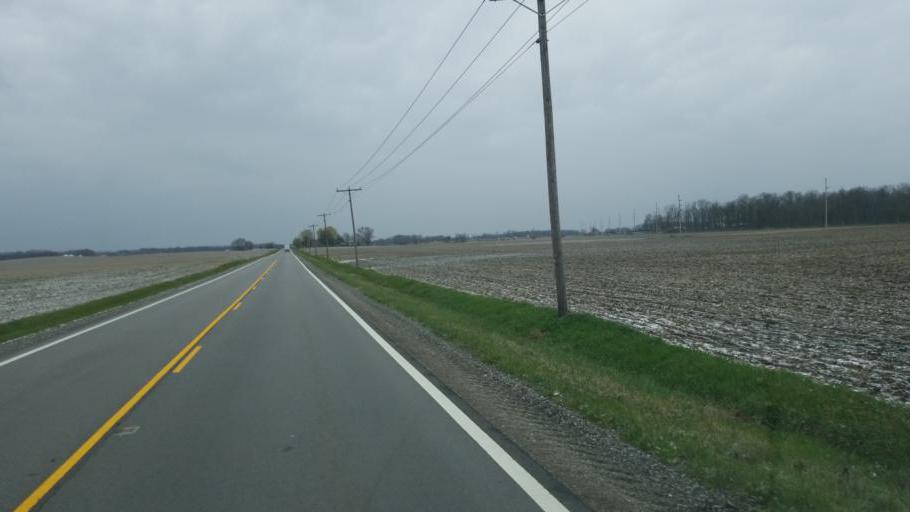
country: US
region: Ohio
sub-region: Marion County
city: Marion
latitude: 40.4926
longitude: -83.0665
